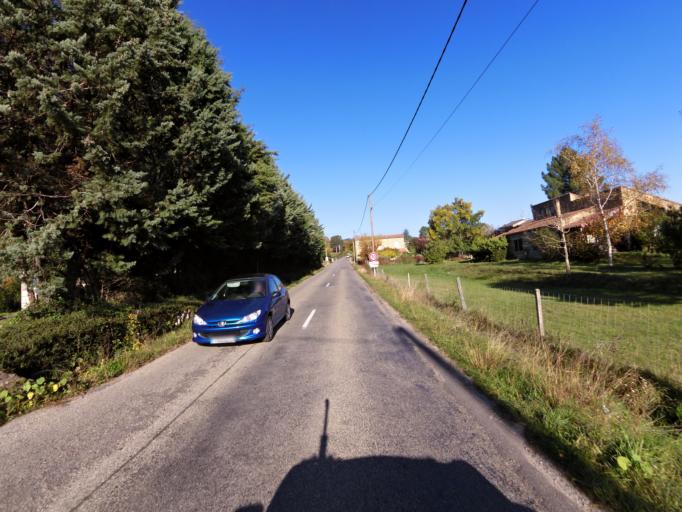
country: FR
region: Rhone-Alpes
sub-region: Departement de l'Ardeche
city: Lablachere
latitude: 44.4661
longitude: 4.2084
